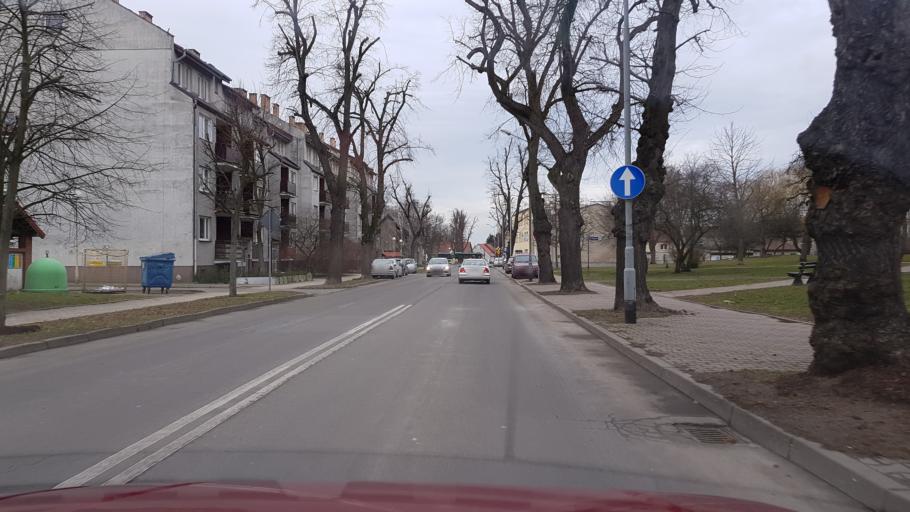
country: PL
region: West Pomeranian Voivodeship
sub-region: Powiat policki
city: Police
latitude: 53.5503
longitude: 14.5716
